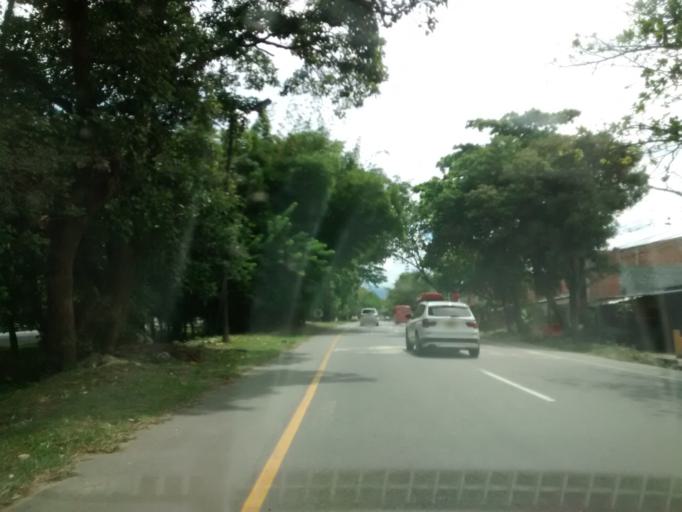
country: CO
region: Tolima
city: Ibague
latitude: 4.4019
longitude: -75.1507
